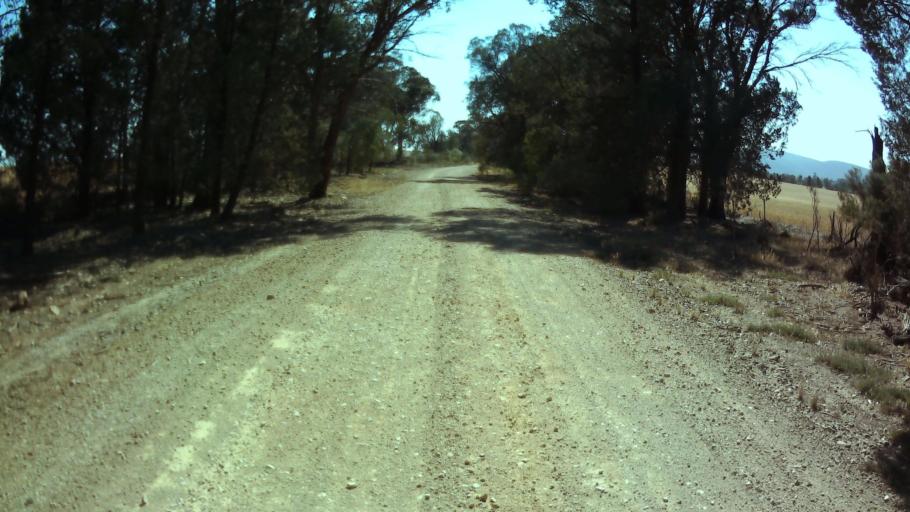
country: AU
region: New South Wales
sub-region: Weddin
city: Grenfell
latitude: -33.9047
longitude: 147.8580
